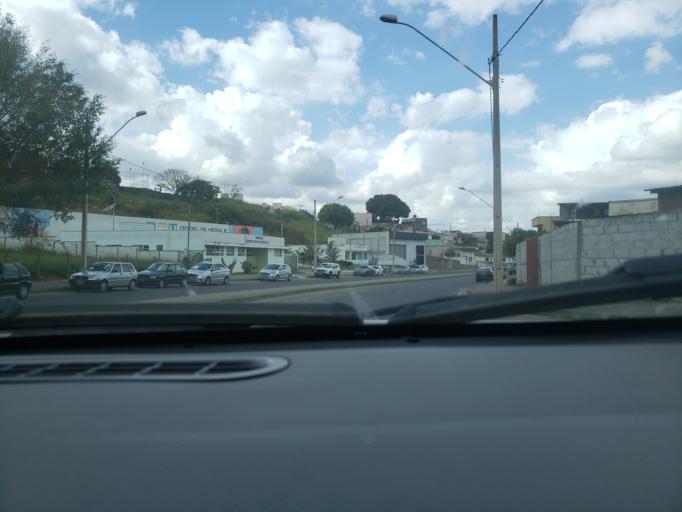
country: BR
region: Minas Gerais
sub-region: Campo Belo
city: Campo Belo
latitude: -20.9009
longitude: -45.2721
